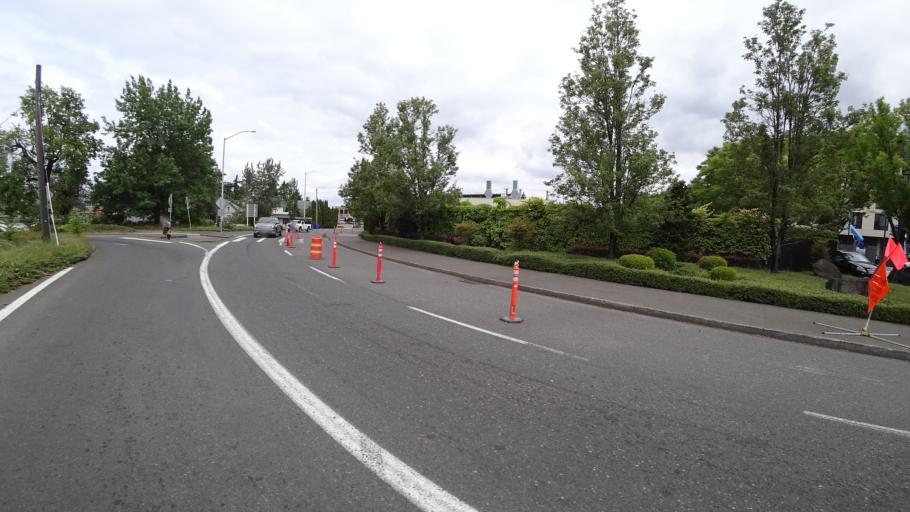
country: US
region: Oregon
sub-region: Multnomah County
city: Lents
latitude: 45.4793
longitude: -122.5699
